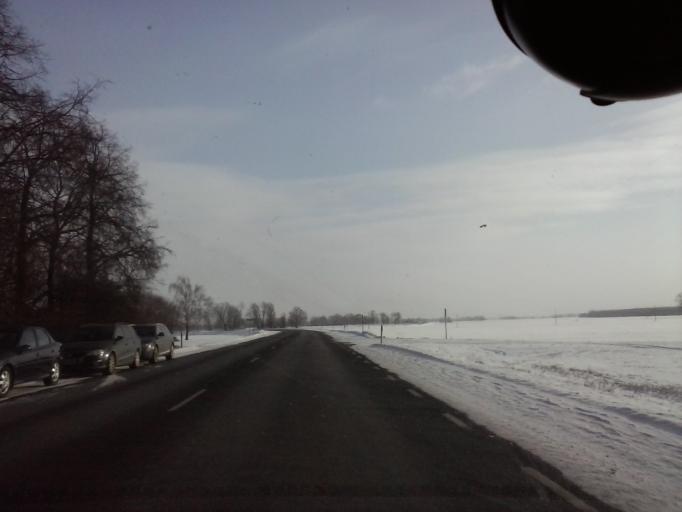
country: EE
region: Tartu
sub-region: Puhja vald
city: Puhja
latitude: 58.3346
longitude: 26.1849
